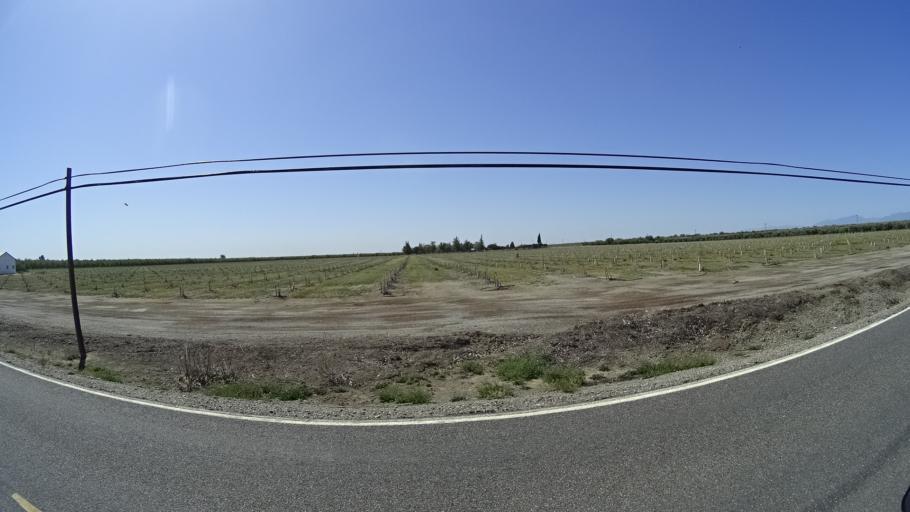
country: US
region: California
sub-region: Glenn County
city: Orland
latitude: 39.7108
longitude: -122.1381
